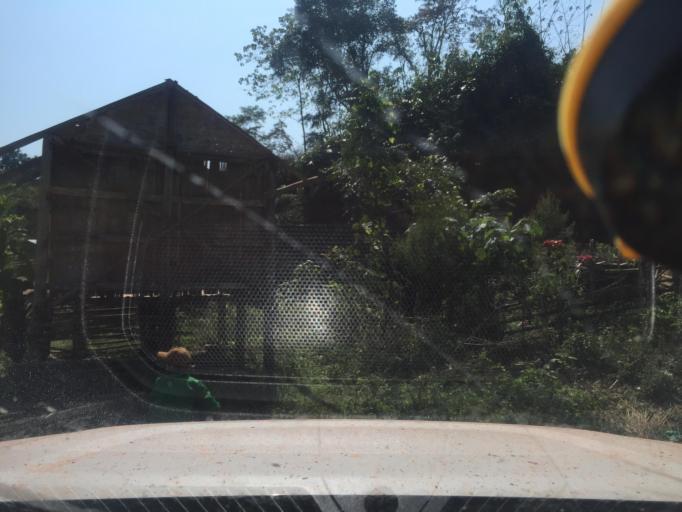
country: LA
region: Phongsali
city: Phongsali
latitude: 21.6496
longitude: 102.4075
